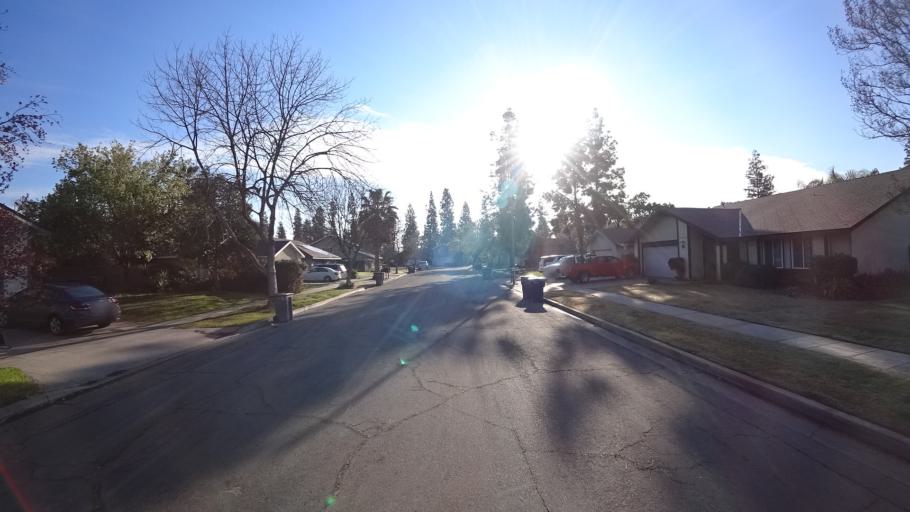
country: US
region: California
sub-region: Fresno County
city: West Park
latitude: 36.8126
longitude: -119.8644
